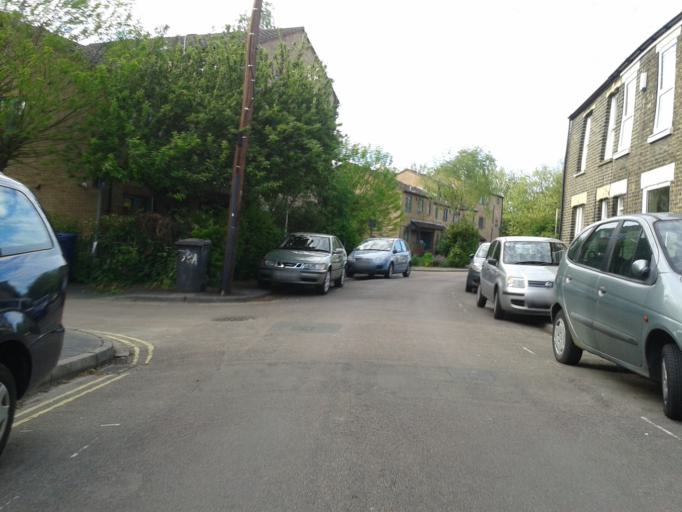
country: GB
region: England
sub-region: Cambridgeshire
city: Cambridge
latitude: 52.1974
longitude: 0.1416
